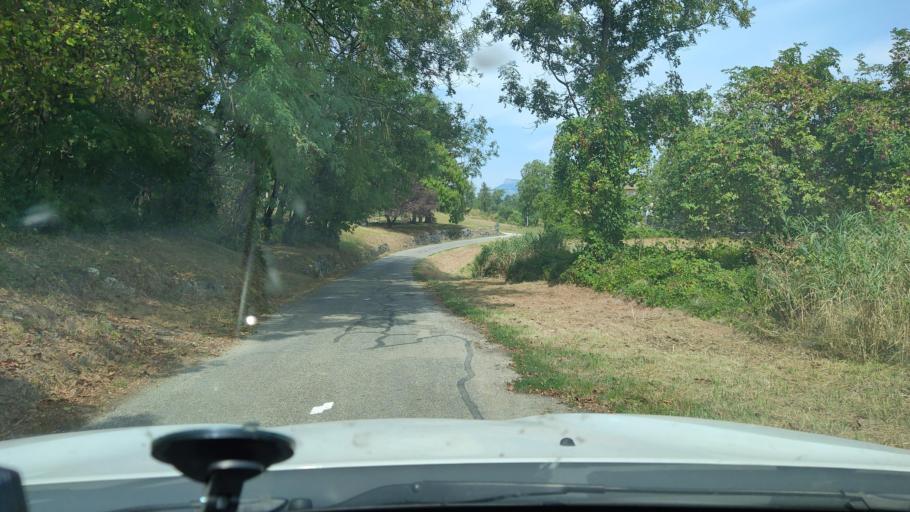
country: FR
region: Rhone-Alpes
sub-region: Departement de la Savoie
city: Les Marches
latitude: 45.5038
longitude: 5.9828
